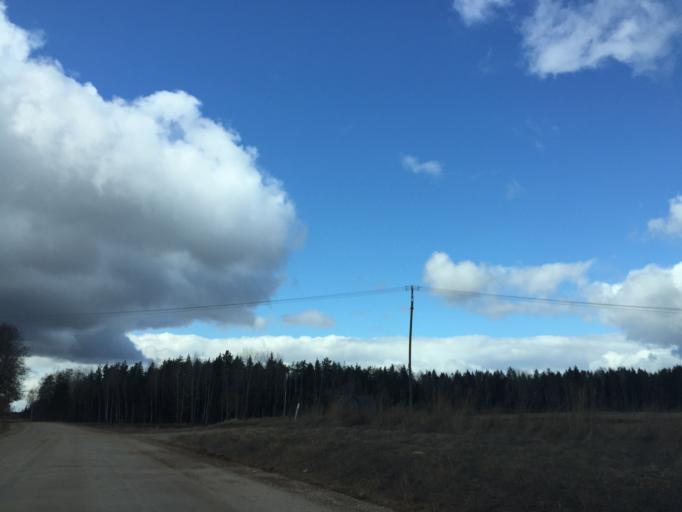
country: LV
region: Akniste
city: Akniste
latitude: 56.1173
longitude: 25.8568
